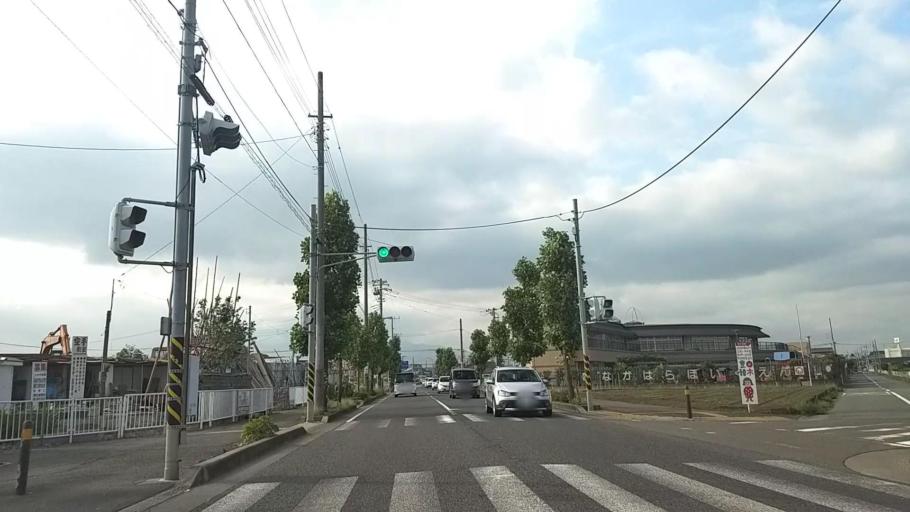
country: JP
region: Kanagawa
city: Hiratsuka
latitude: 35.3535
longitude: 139.3290
